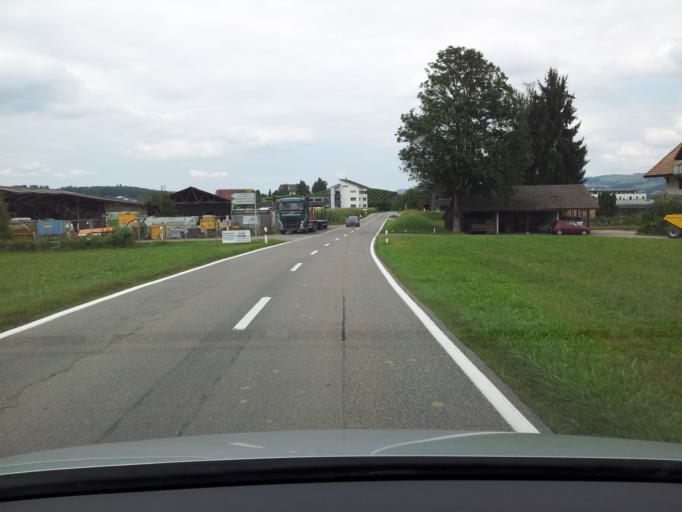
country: CH
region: Lucerne
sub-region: Sursee District
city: Oberkirch
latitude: 47.1482
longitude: 8.1154
